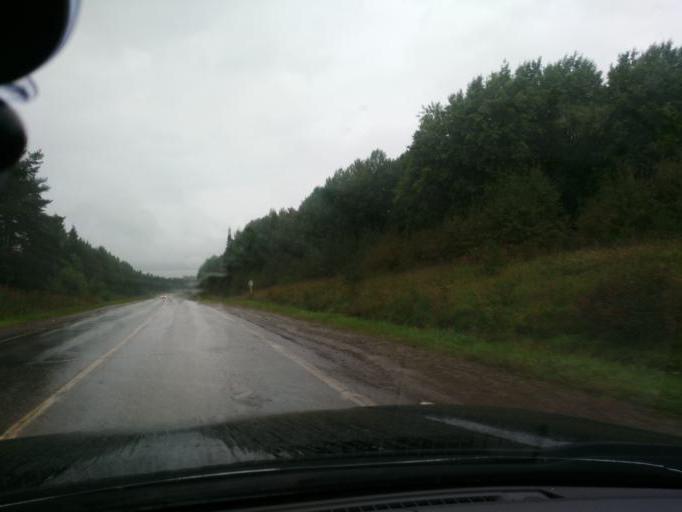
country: RU
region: Perm
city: Osa
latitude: 57.3245
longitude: 55.6103
